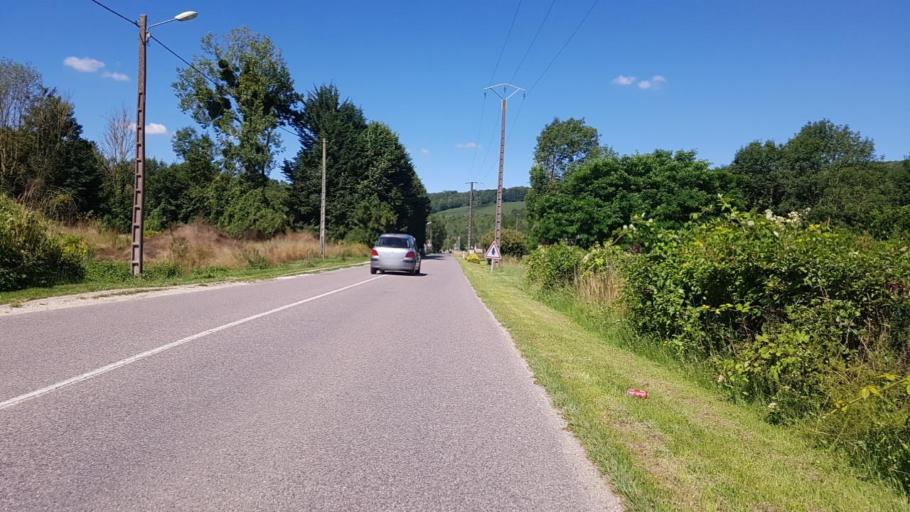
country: FR
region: Ile-de-France
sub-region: Departement de Seine-et-Marne
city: Saacy-sur-Marne
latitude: 48.9782
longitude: 3.2324
